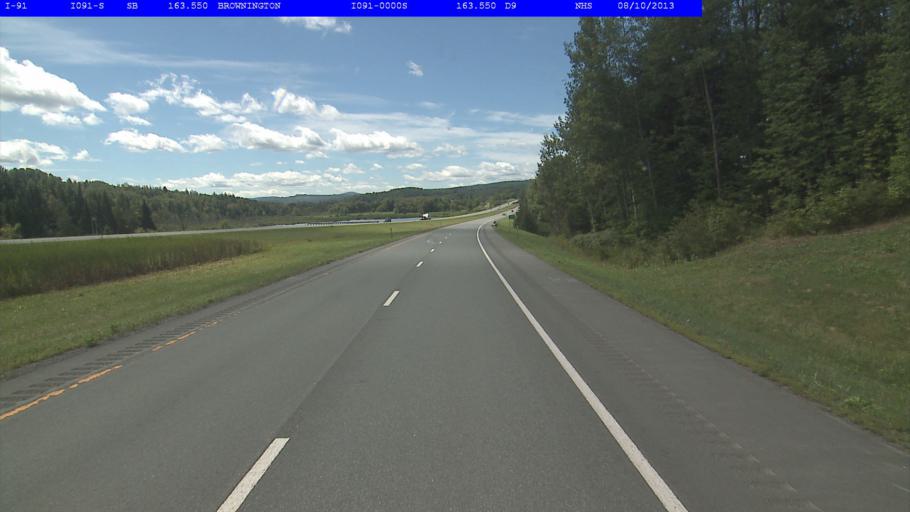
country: US
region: Vermont
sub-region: Orleans County
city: Newport
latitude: 44.8344
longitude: -72.1965
